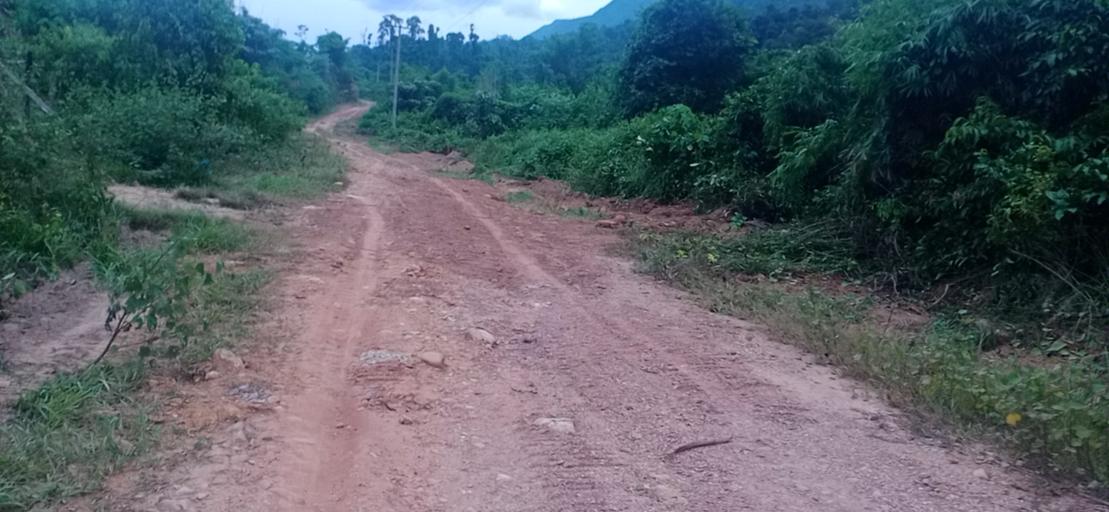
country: TH
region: Changwat Bueng Kan
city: Pak Khat
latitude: 18.5581
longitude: 103.2365
